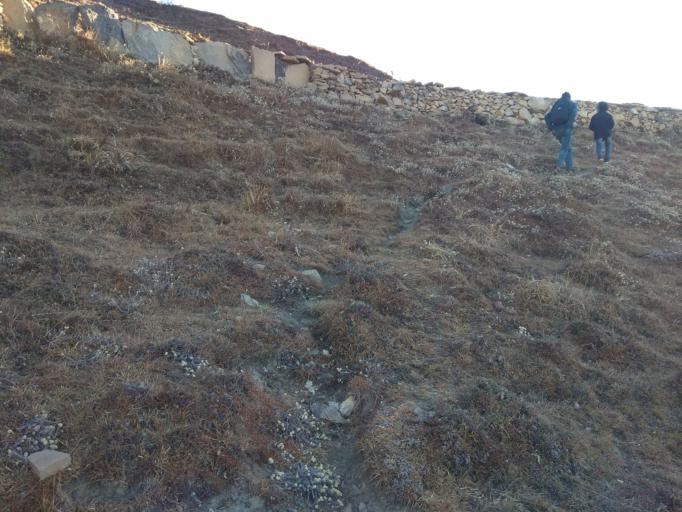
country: NP
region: Far Western
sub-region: Seti Zone
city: Achham
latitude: 29.2768
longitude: 81.6483
